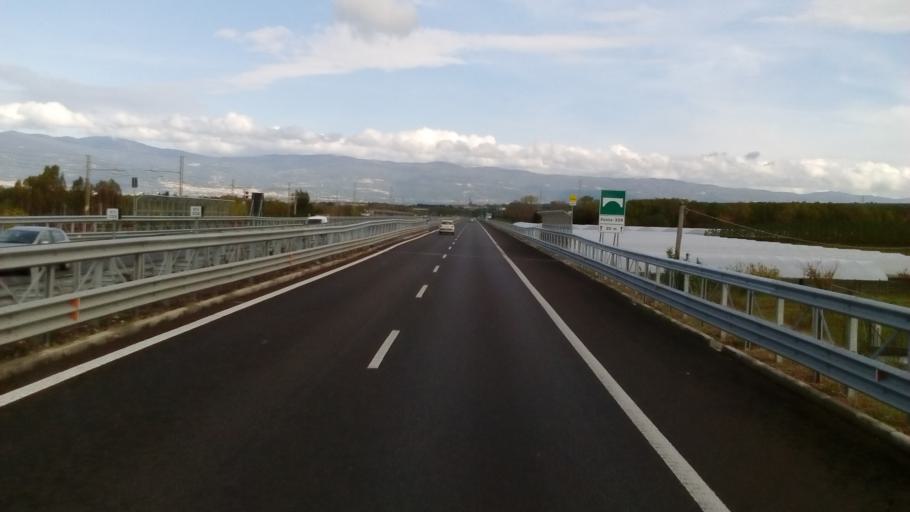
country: IT
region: Calabria
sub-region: Provincia di Catanzaro
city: Acconia
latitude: 38.8470
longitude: 16.2662
